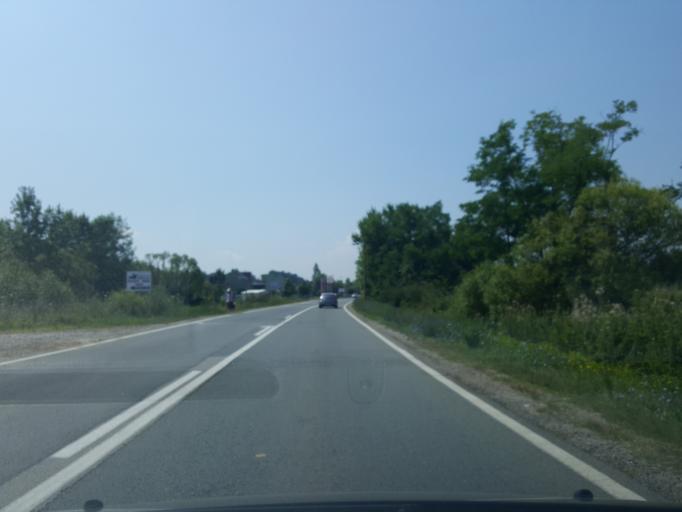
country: RS
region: Central Serbia
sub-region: Belgrade
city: Mladenovac
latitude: 44.4961
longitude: 20.6564
